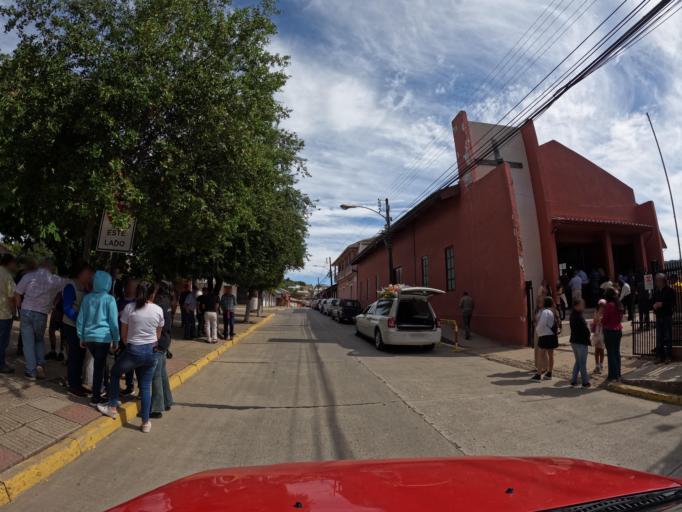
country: CL
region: Maule
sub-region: Provincia de Talca
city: Constitucion
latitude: -35.0937
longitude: -72.0184
